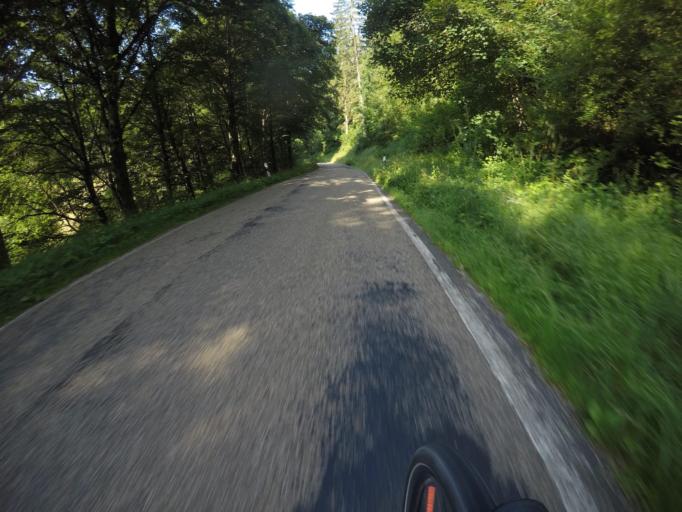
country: DE
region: Baden-Wuerttemberg
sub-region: Regierungsbezirk Stuttgart
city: Motzingen
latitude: 48.4604
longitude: 8.7694
